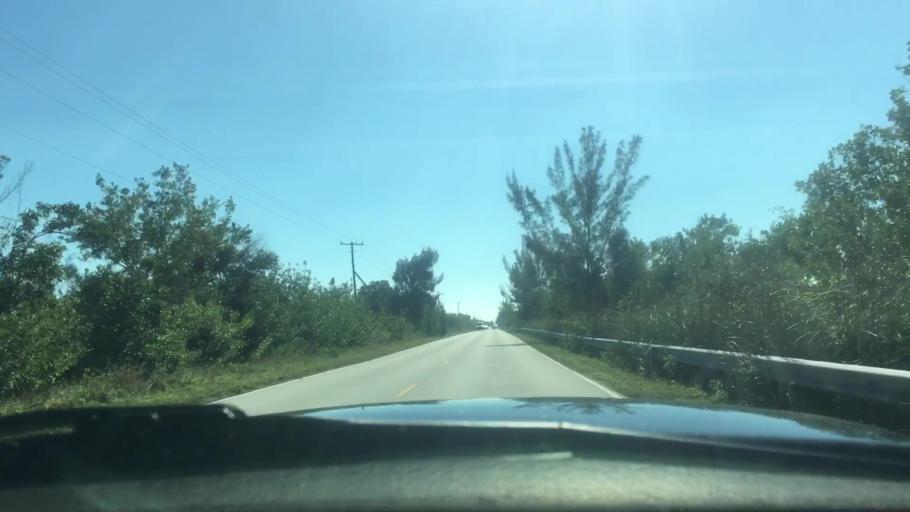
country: US
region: Florida
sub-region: Miami-Dade County
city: Florida City
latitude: 25.3628
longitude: -80.4272
